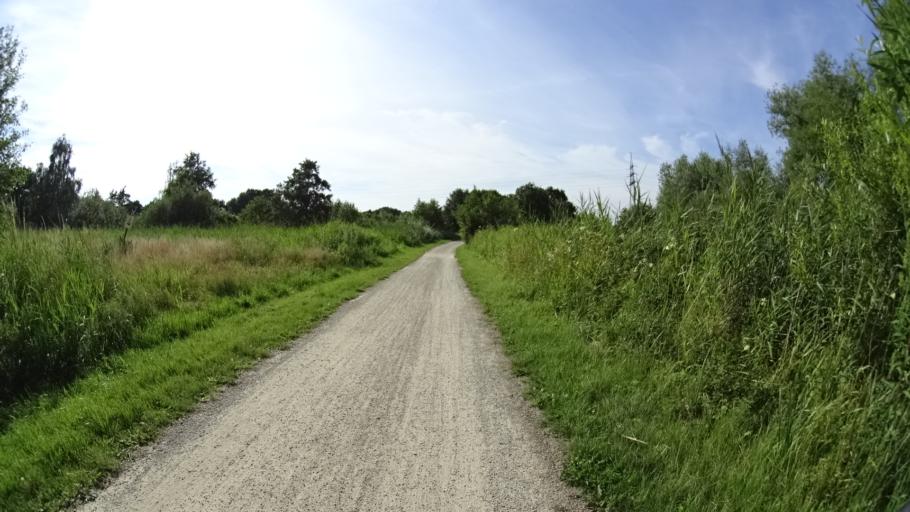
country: DE
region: Lower Saxony
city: Adendorf
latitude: 53.2796
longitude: 10.4115
